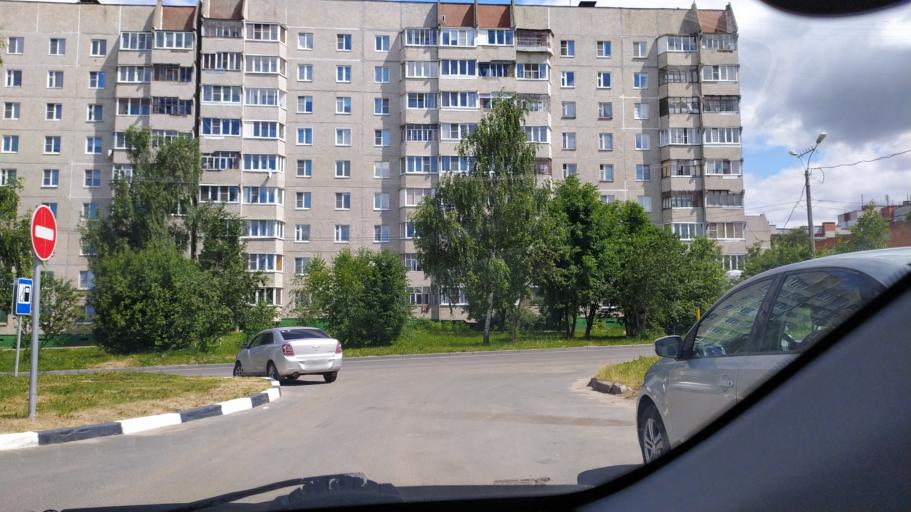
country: RU
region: Chuvashia
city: Novyye Lapsary
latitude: 56.1167
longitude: 47.1761
